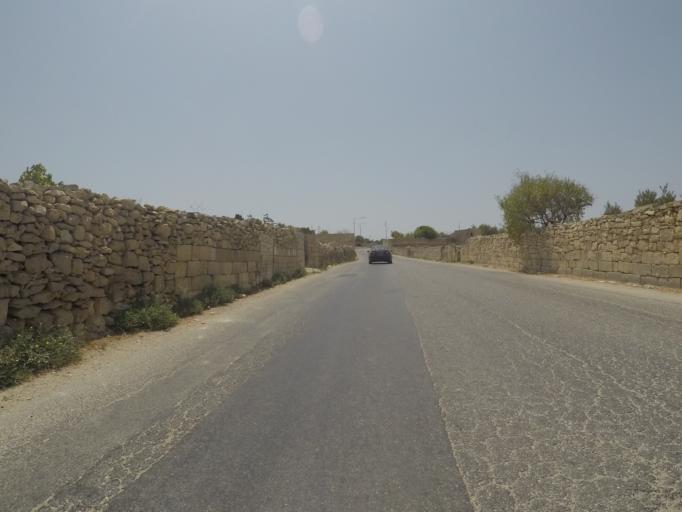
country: MT
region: Is-Siggiewi
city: Siggiewi
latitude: 35.8443
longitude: 14.4344
